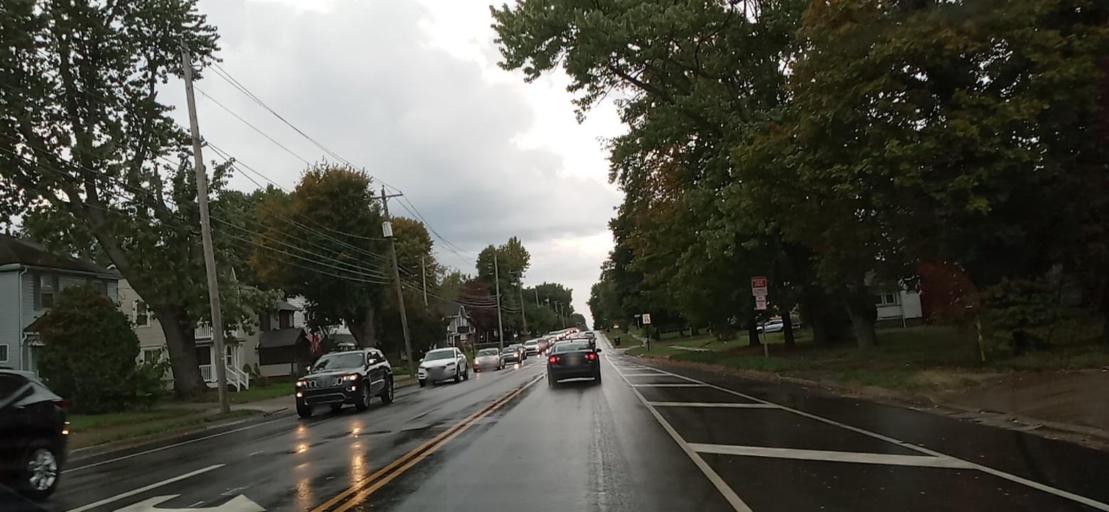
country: US
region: Ohio
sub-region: Summit County
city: Akron
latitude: 41.0842
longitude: -81.5694
